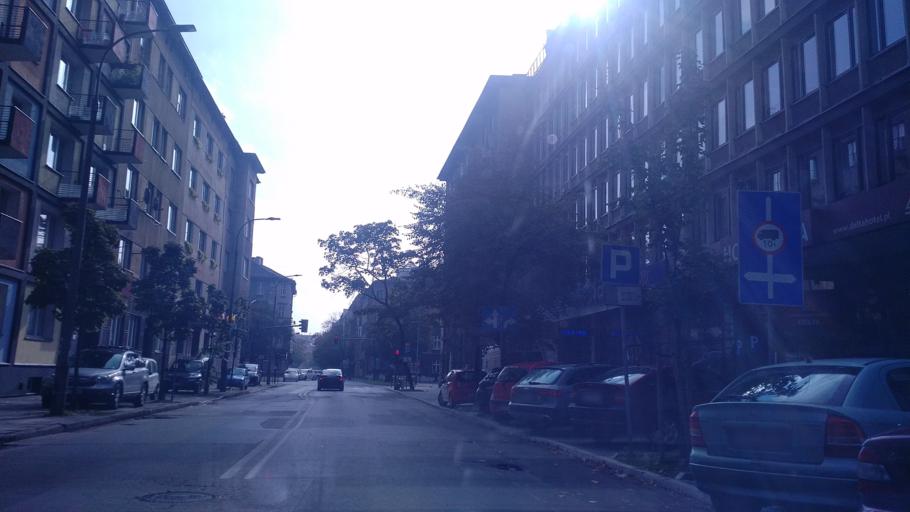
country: PL
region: Lesser Poland Voivodeship
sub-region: Krakow
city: Krakow
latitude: 50.0732
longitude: 19.9303
